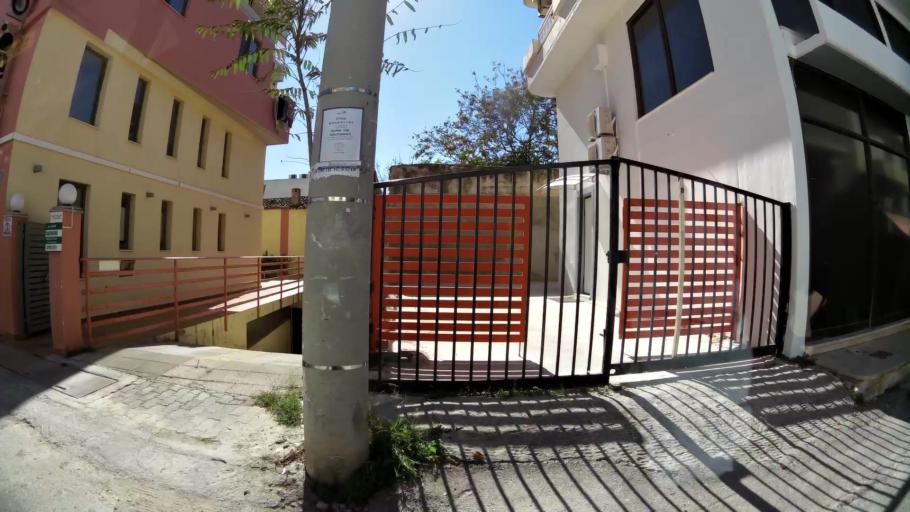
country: GR
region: Attica
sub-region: Nomarchia Anatolikis Attikis
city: Markopoulo
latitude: 37.8838
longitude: 23.9331
